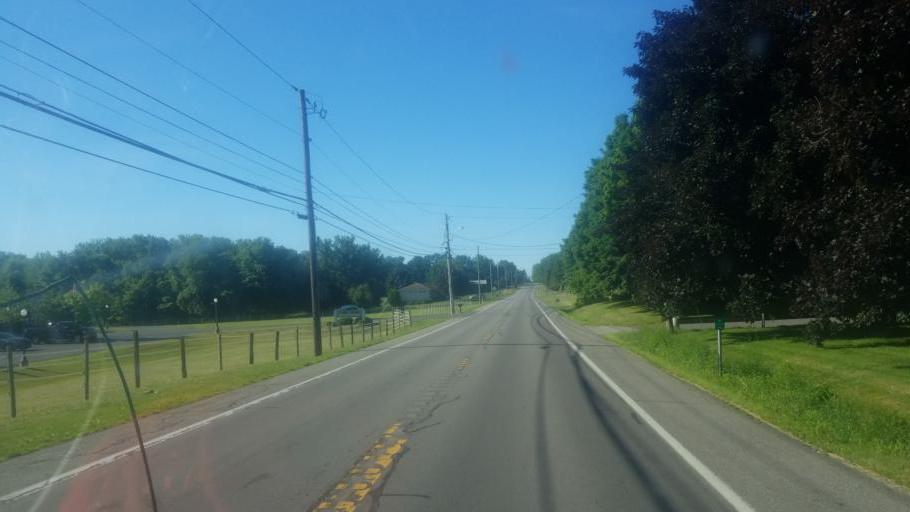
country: US
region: New York
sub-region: Wayne County
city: Newark
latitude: 43.0197
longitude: -77.0942
